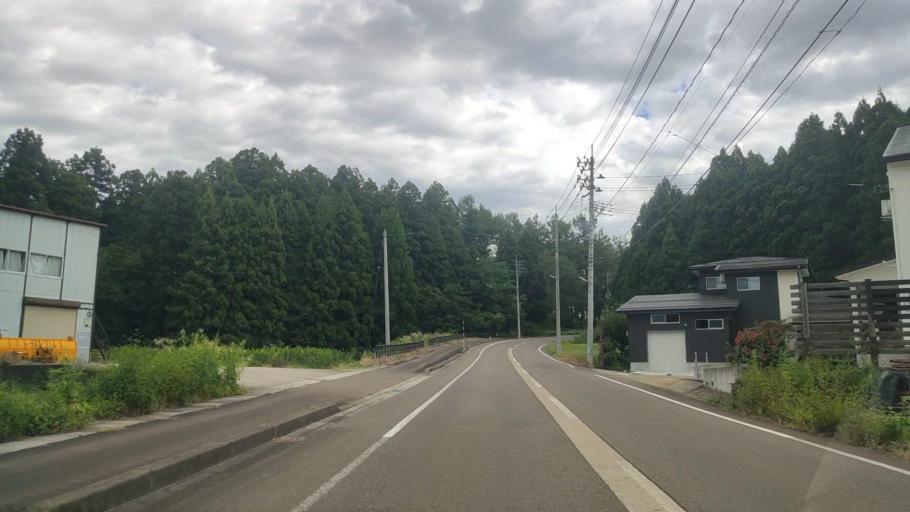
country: JP
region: Niigata
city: Arai
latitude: 37.0127
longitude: 138.2517
